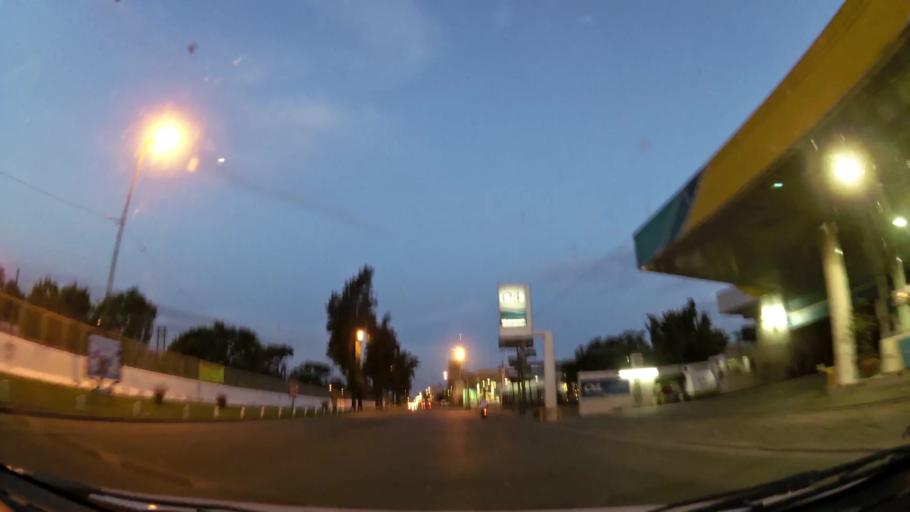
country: AR
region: Buenos Aires
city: Ituzaingo
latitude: -34.6625
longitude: -58.6748
